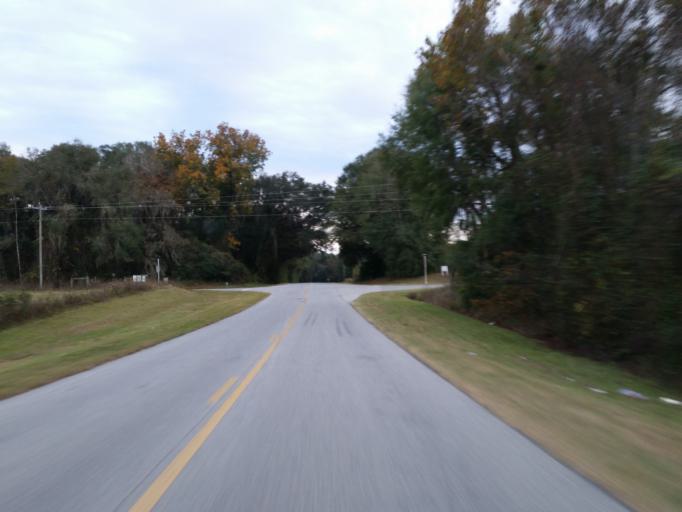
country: US
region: Florida
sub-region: Hamilton County
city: Jasper
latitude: 30.5275
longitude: -83.1026
